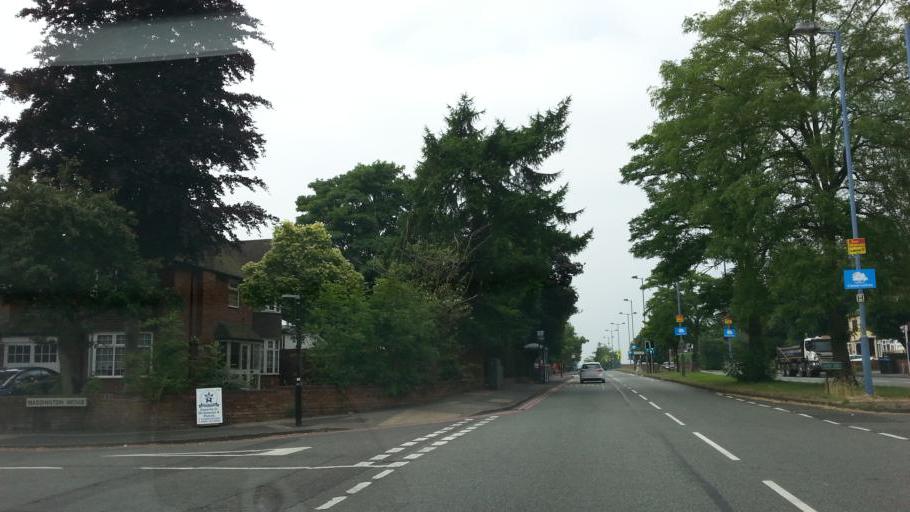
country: GB
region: England
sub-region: City and Borough of Birmingham
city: Hockley
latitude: 52.5450
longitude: -1.9407
